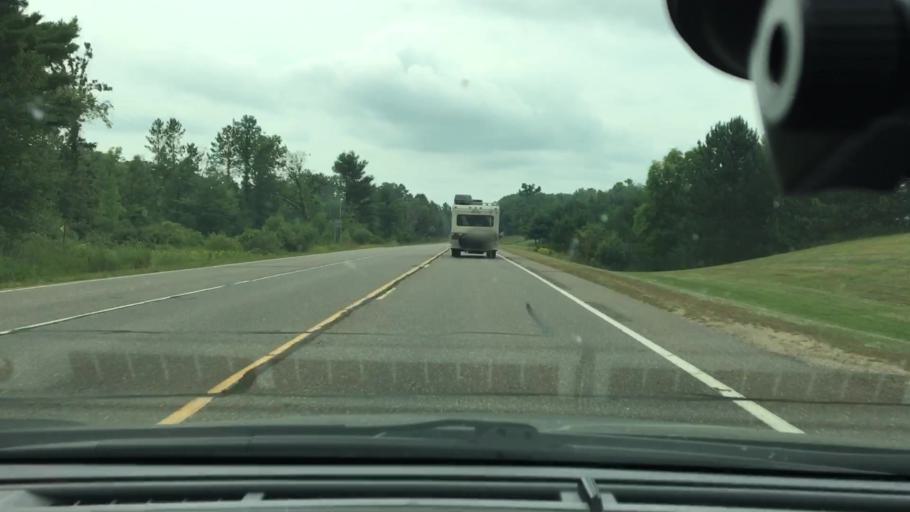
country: US
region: Minnesota
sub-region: Crow Wing County
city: Crosby
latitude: 46.4243
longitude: -93.8733
